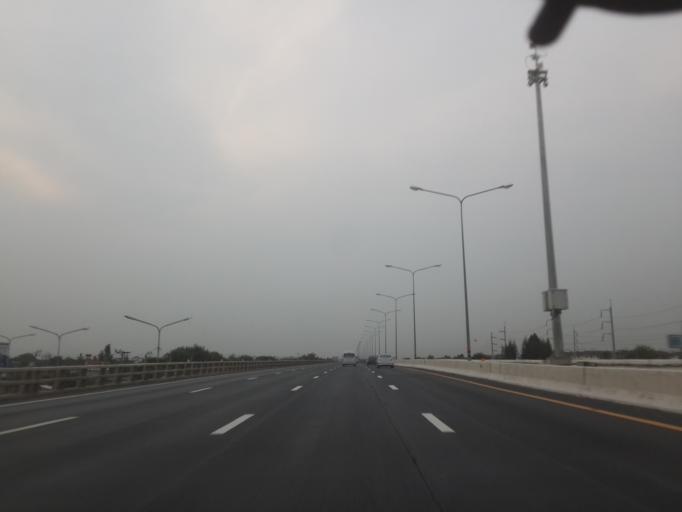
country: TH
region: Bangkok
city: Lat Krabang
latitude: 13.7108
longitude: 100.8197
